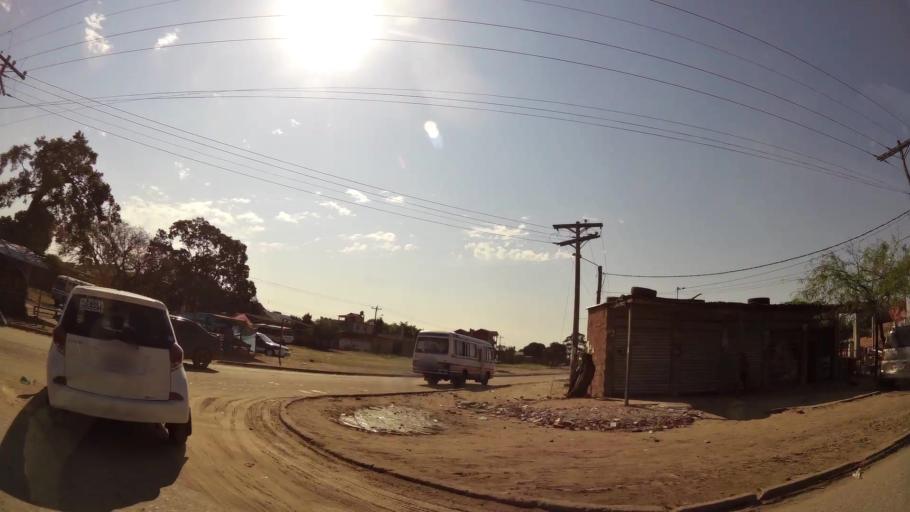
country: BO
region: Santa Cruz
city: Cotoca
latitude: -17.8182
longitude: -63.1185
